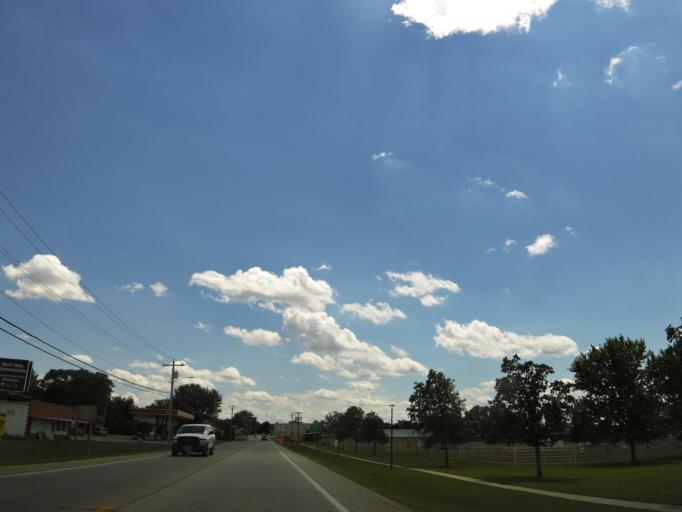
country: US
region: Iowa
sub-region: Buchanan County
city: Independence
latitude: 42.4811
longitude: -91.8894
